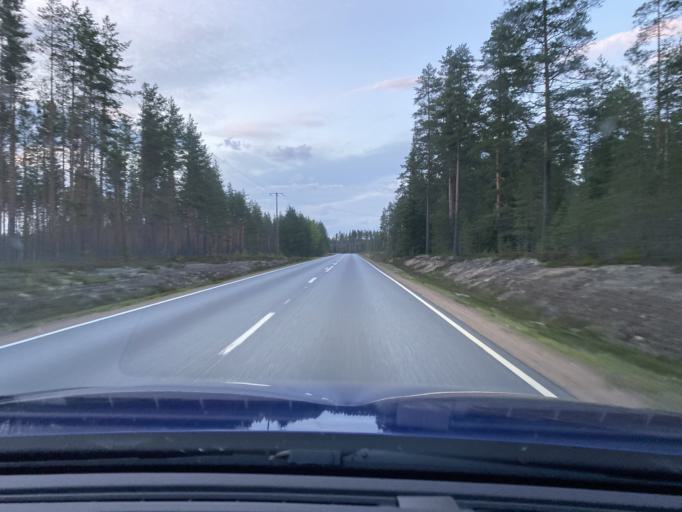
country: FI
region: Satakunta
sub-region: Pohjois-Satakunta
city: Honkajoki
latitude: 62.1895
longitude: 22.2968
